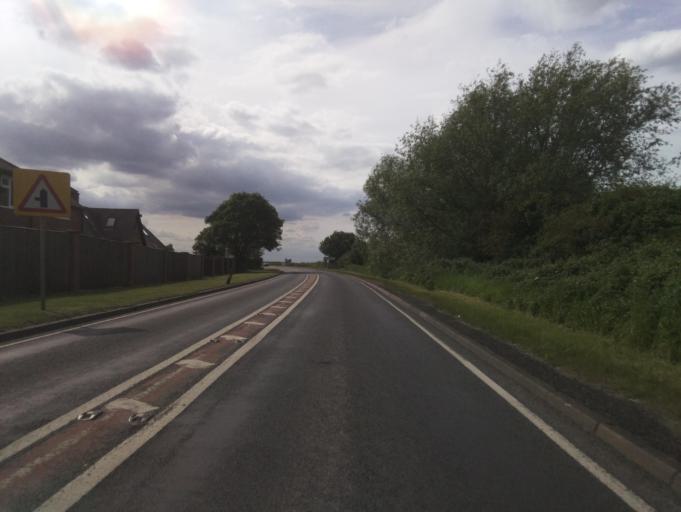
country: GB
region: England
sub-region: Worcestershire
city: Pershore
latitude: 52.1001
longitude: -2.0199
